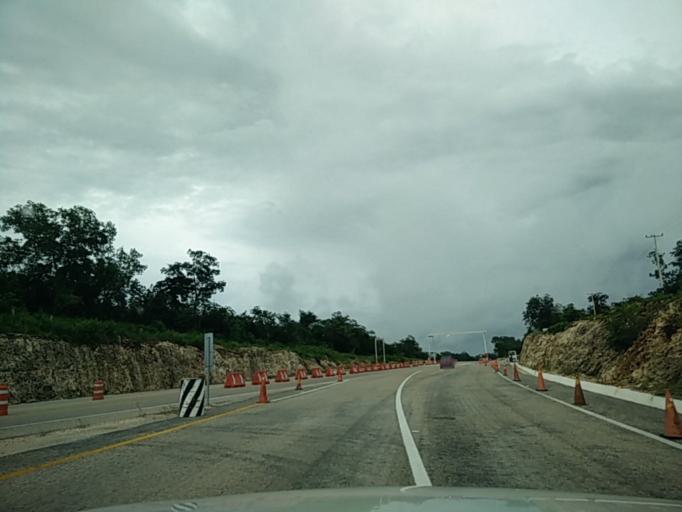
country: MX
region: Quintana Roo
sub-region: Lazaro Cardenas
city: El Tintal
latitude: 20.8898
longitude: -87.4348
